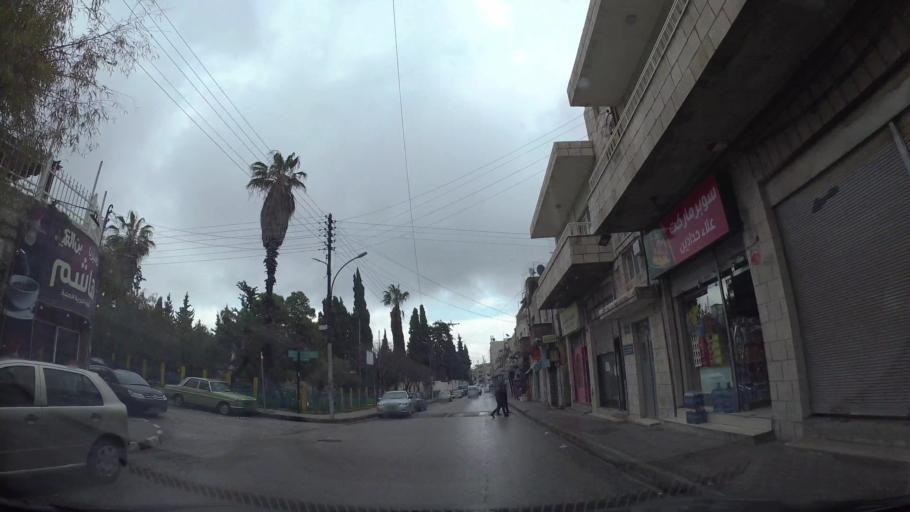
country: JO
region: Amman
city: Amman
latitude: 31.9482
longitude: 35.9241
